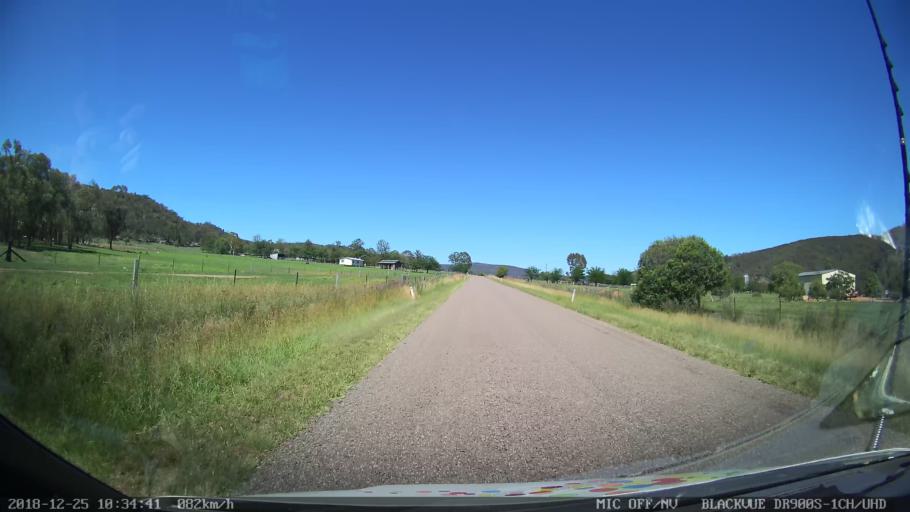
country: AU
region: New South Wales
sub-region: Upper Hunter Shire
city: Merriwa
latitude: -32.3935
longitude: 150.4048
